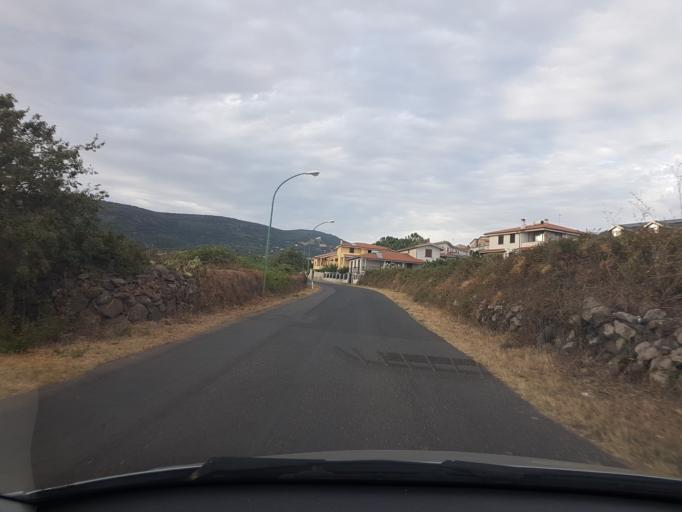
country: IT
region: Sardinia
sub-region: Provincia di Oristano
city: Seneghe
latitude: 40.0799
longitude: 8.6067
